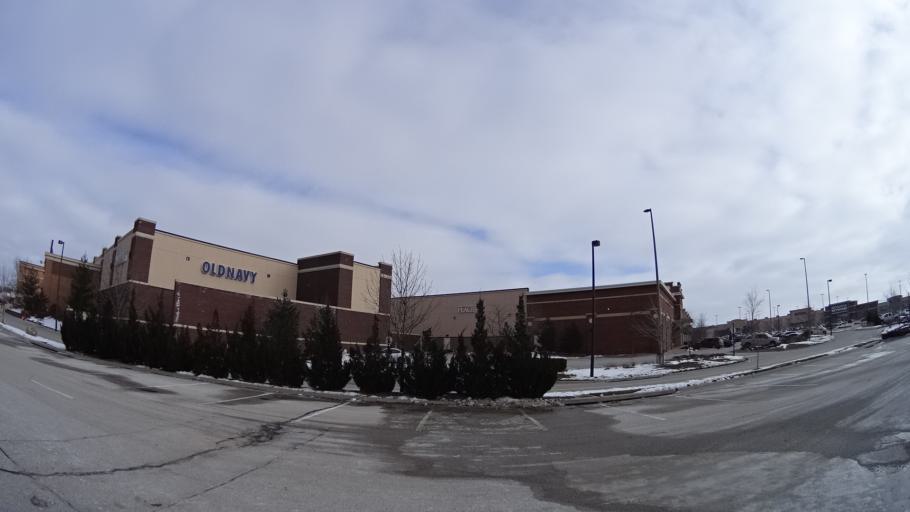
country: US
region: Nebraska
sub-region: Sarpy County
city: Papillion
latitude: 41.1355
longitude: -96.0300
